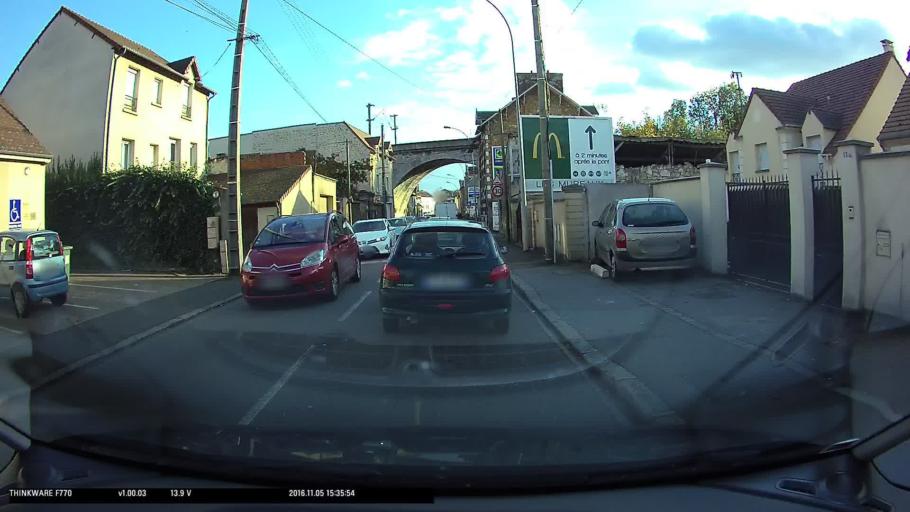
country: FR
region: Ile-de-France
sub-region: Departement des Yvelines
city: Meulan-en-Yvelines
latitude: 49.0070
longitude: 1.9055
